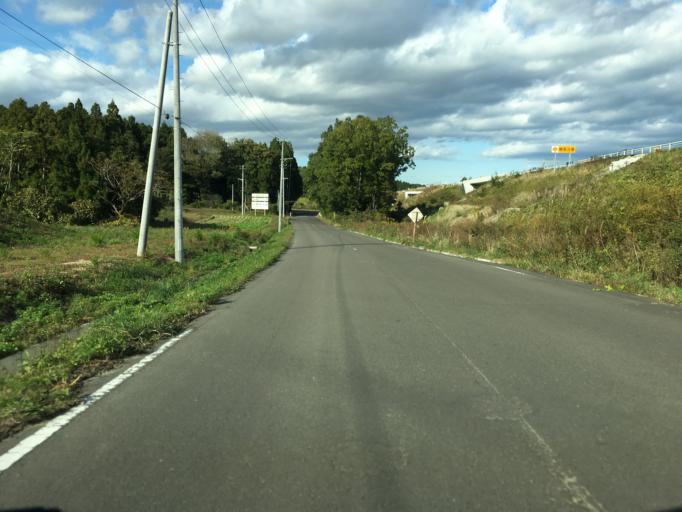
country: JP
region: Miyagi
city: Marumori
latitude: 37.8585
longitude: 140.8812
